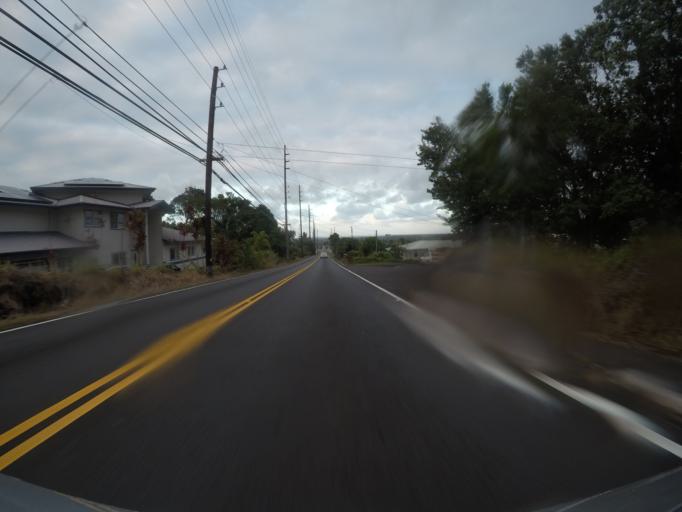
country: US
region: Hawaii
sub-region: Hawaii County
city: Hilo
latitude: 19.6835
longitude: -155.0856
